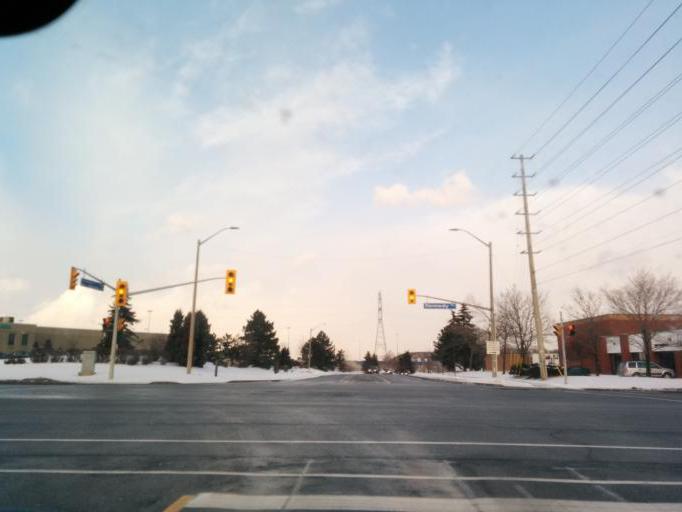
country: CA
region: Ontario
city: Mississauga
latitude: 43.6341
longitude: -79.6665
